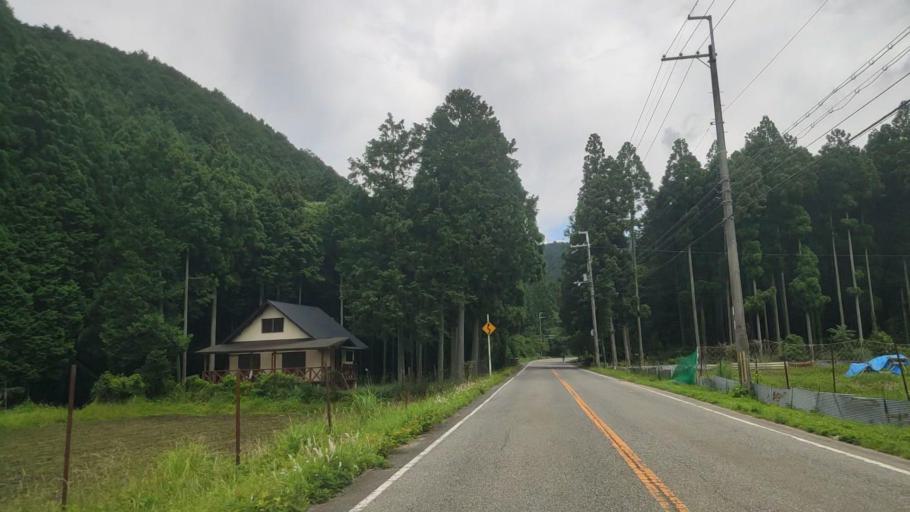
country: JP
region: Kyoto
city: Fukuchiyama
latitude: 35.2035
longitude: 134.9377
